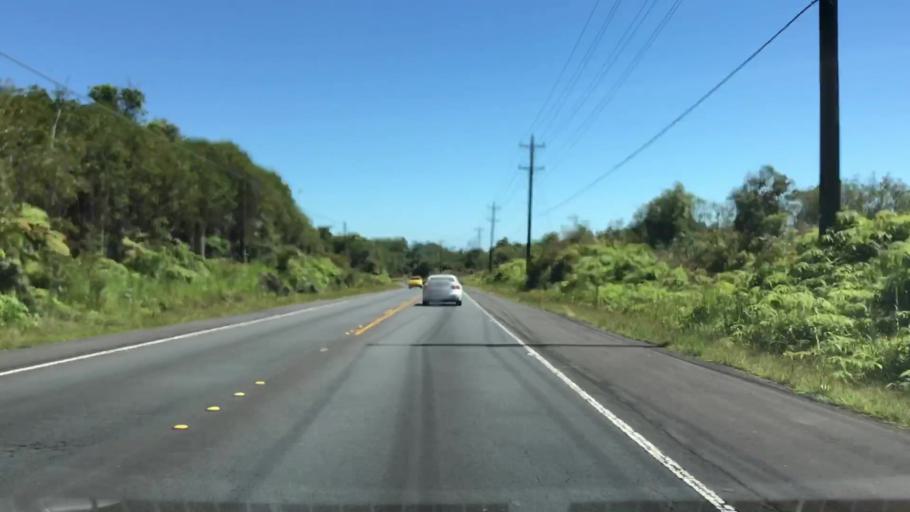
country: US
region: Hawaii
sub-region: Hawaii County
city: Volcano
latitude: 19.4642
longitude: -155.1673
